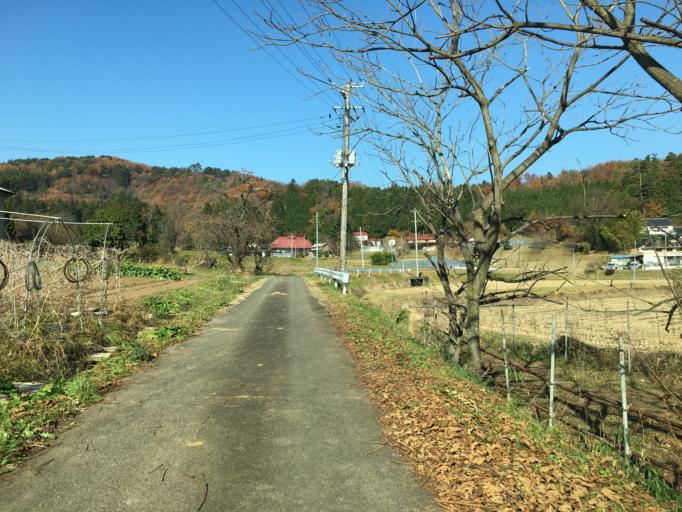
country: JP
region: Fukushima
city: Nihommatsu
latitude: 37.5732
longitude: 140.3770
